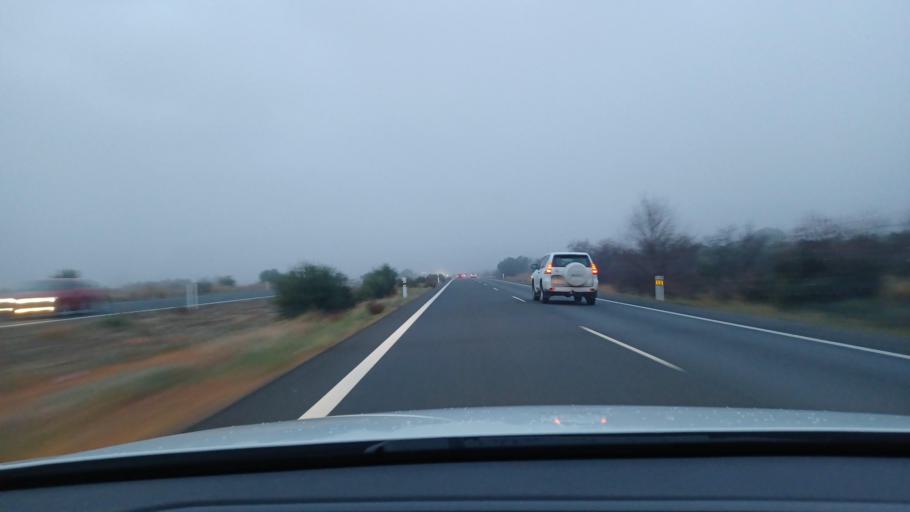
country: ES
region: Valencia
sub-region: Provincia de Valencia
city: Mogente
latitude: 38.8585
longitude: -0.8110
